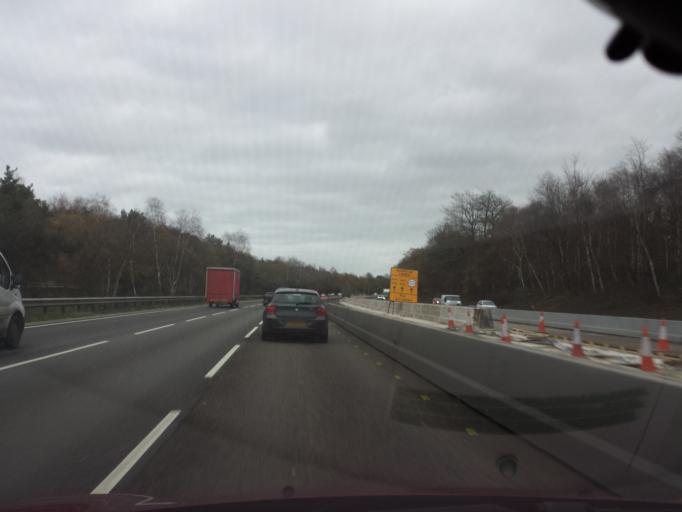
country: GB
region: England
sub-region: Surrey
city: Virginia Water
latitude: 51.3834
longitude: -0.5877
